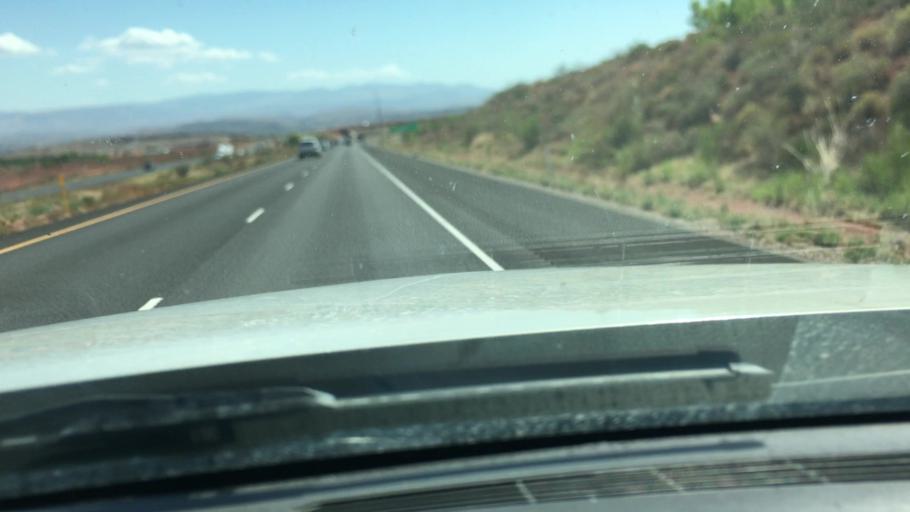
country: US
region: Utah
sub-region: Washington County
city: Washington
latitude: 37.1524
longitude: -113.4817
